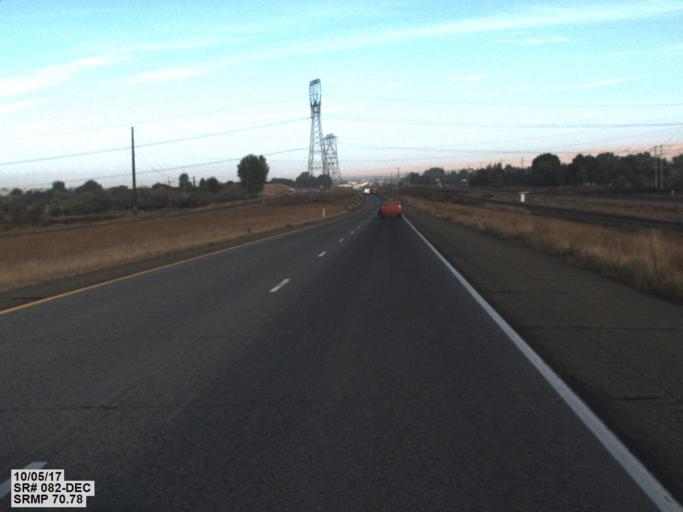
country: US
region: Washington
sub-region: Yakima County
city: Grandview
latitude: 46.2899
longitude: -119.9497
